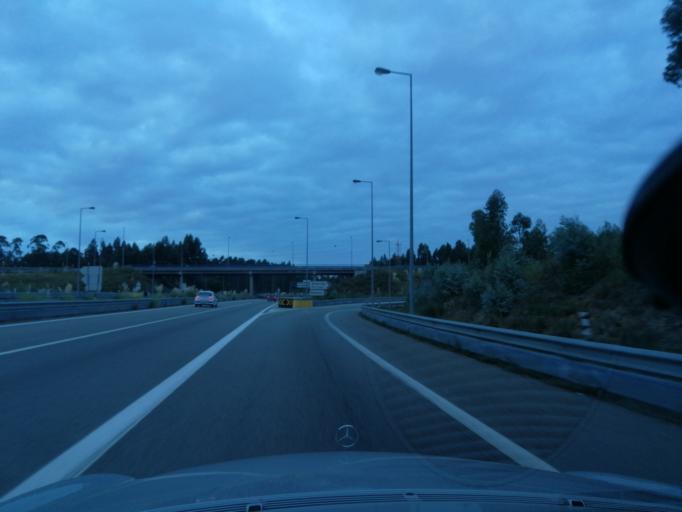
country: PT
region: Aveiro
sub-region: Estarreja
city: Beduido
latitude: 40.7843
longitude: -8.5623
